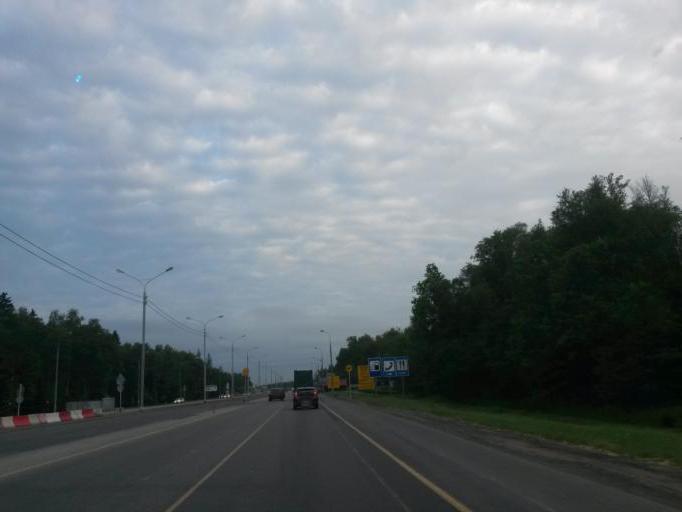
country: RU
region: Moskovskaya
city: Lyubuchany
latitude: 55.1961
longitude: 37.5345
